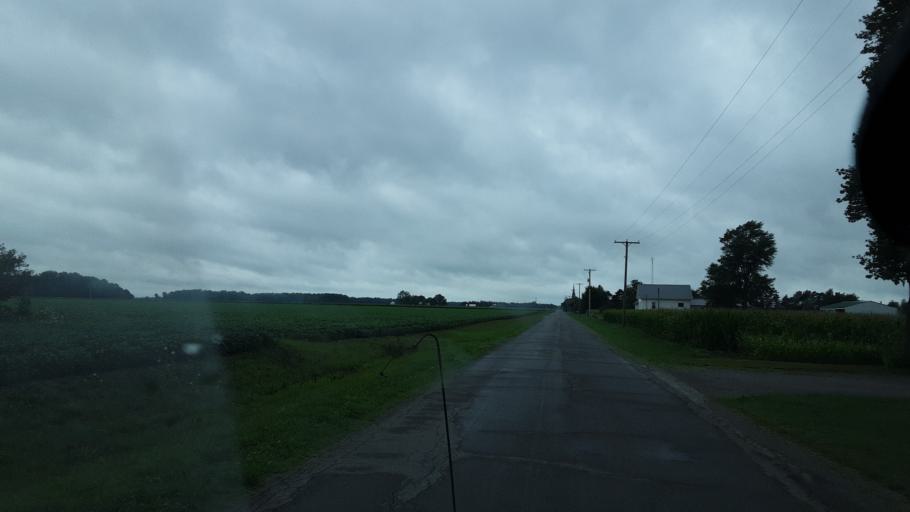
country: US
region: Ohio
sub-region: Van Wert County
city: Convoy
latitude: 40.8223
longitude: -84.6929
